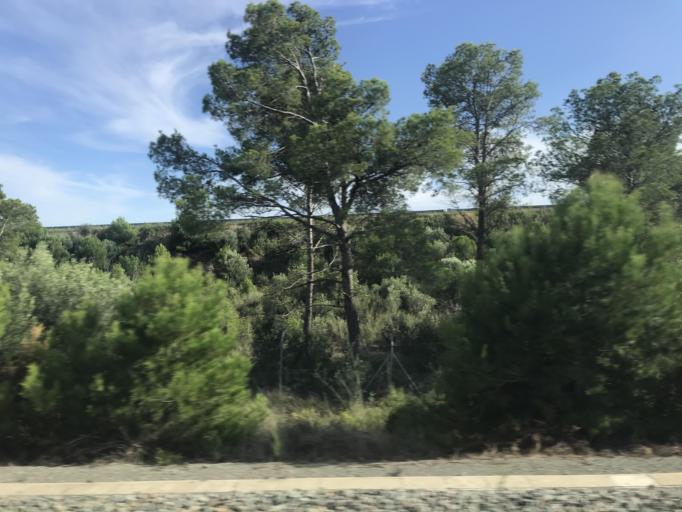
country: ES
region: Catalonia
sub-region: Provincia de Tarragona
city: Vilanova d'Escornalbou
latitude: 41.0407
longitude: 0.9569
